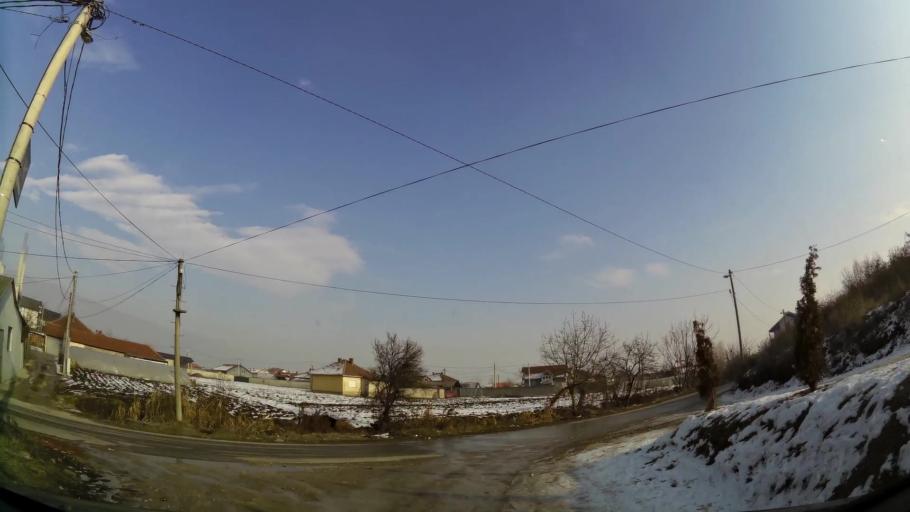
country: MK
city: Creshevo
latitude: 42.0183
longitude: 21.5071
